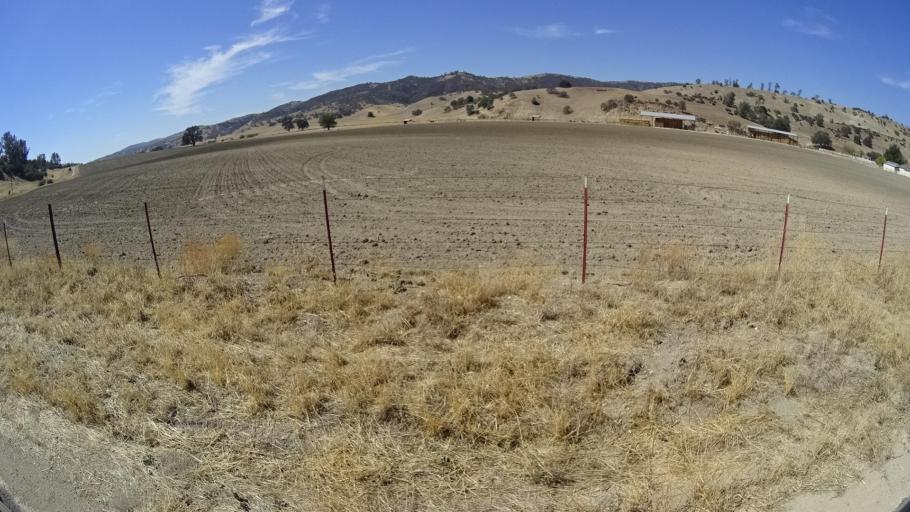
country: US
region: California
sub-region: San Luis Obispo County
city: San Miguel
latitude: 35.9544
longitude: -120.6538
